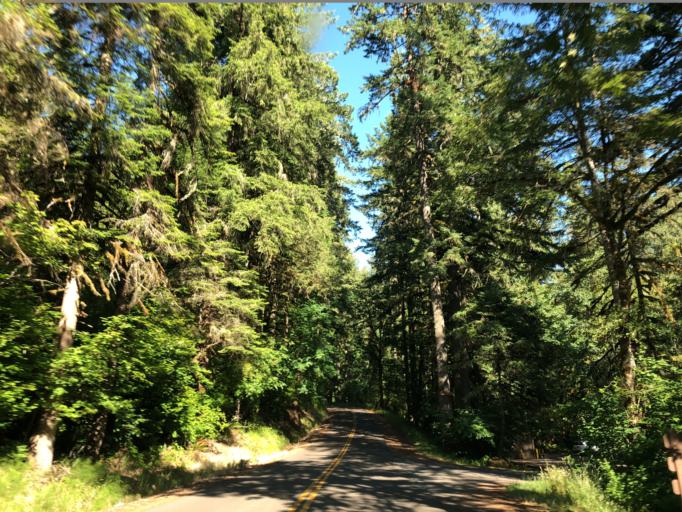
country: US
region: Oregon
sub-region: Linn County
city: Sweet Home
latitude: 44.4647
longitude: -122.6832
